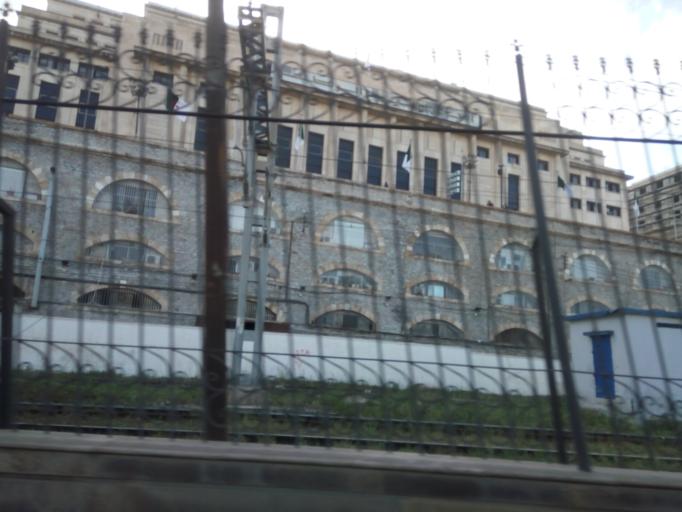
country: DZ
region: Alger
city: Algiers
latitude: 36.7762
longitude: 3.0610
